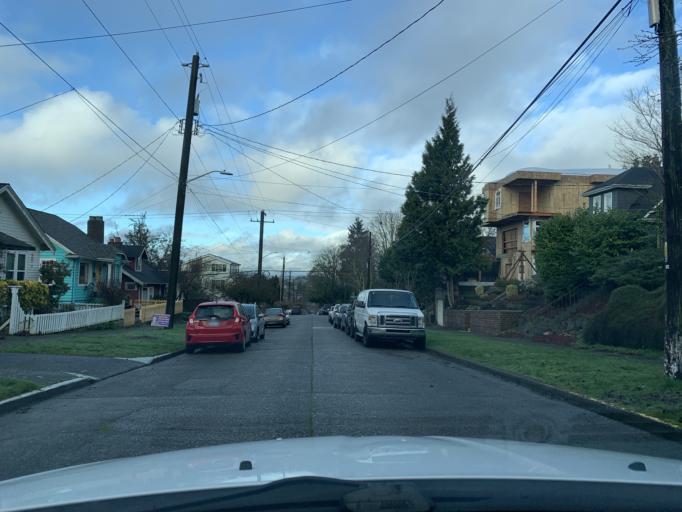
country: US
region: Washington
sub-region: King County
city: Seattle
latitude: 47.6146
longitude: -122.2949
